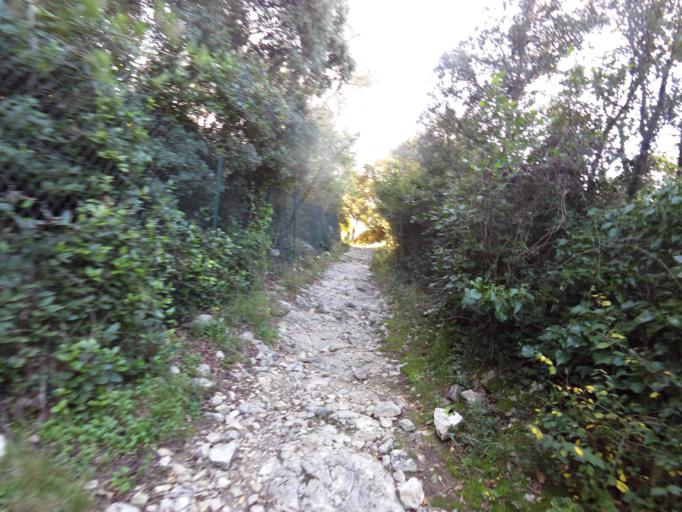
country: FR
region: Languedoc-Roussillon
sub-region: Departement du Gard
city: Aubais
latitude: 43.7580
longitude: 4.1453
